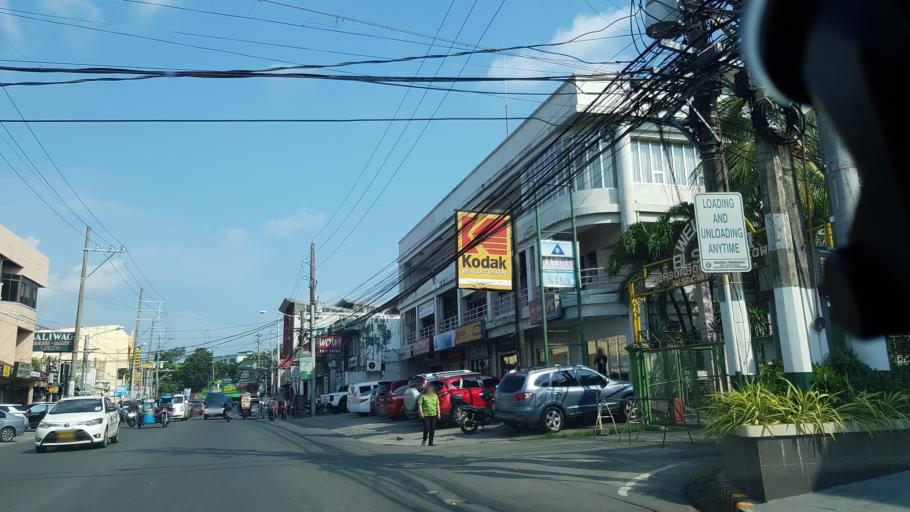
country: PH
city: Sambayanihan People's Village
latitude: 14.4828
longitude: 121.0356
